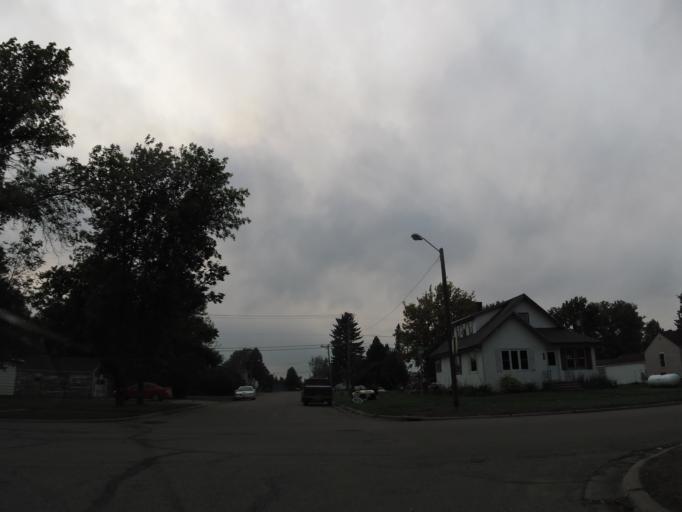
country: US
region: North Dakota
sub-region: Walsh County
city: Grafton
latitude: 48.5593
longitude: -97.1803
